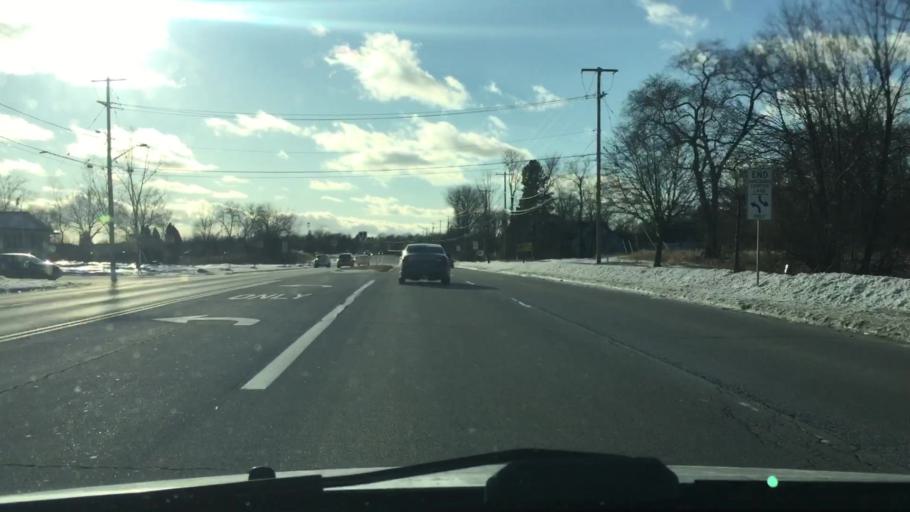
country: US
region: Wisconsin
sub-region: Waukesha County
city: New Berlin
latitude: 42.9849
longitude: -88.0917
